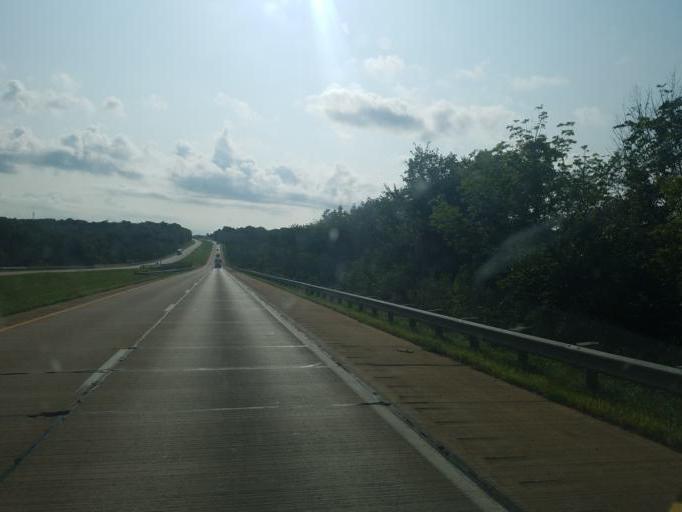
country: US
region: Ohio
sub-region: Ashland County
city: Ashland
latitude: 40.7857
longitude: -82.3281
